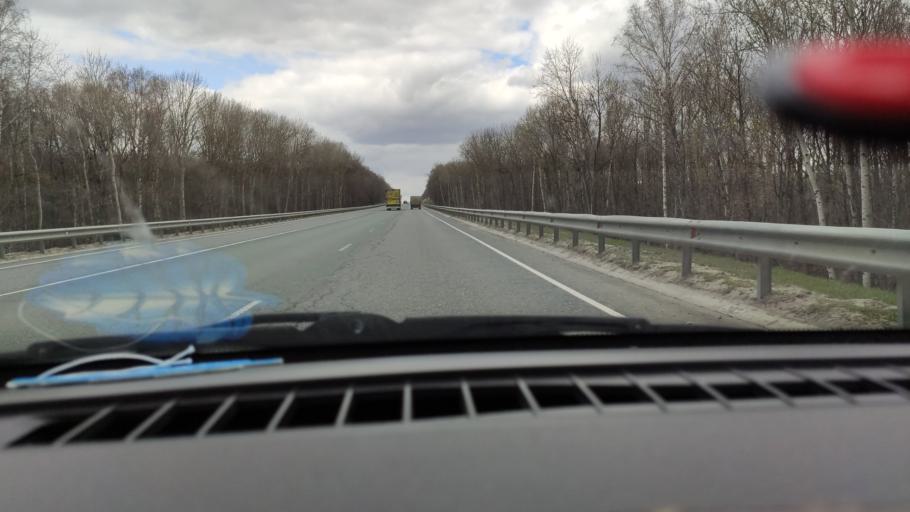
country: RU
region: Saratov
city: Vol'sk
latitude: 52.1071
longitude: 47.4113
